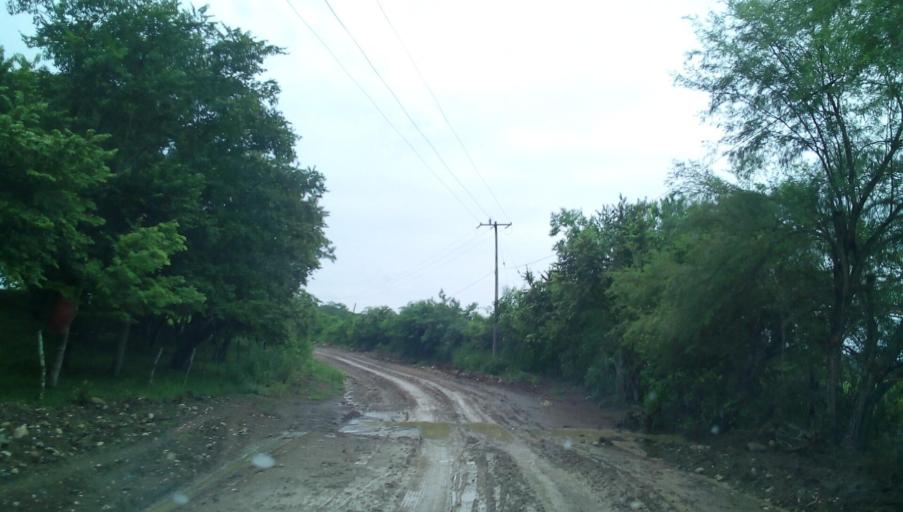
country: MX
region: Veracruz
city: Tempoal de Sanchez
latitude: 21.4482
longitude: -98.4230
